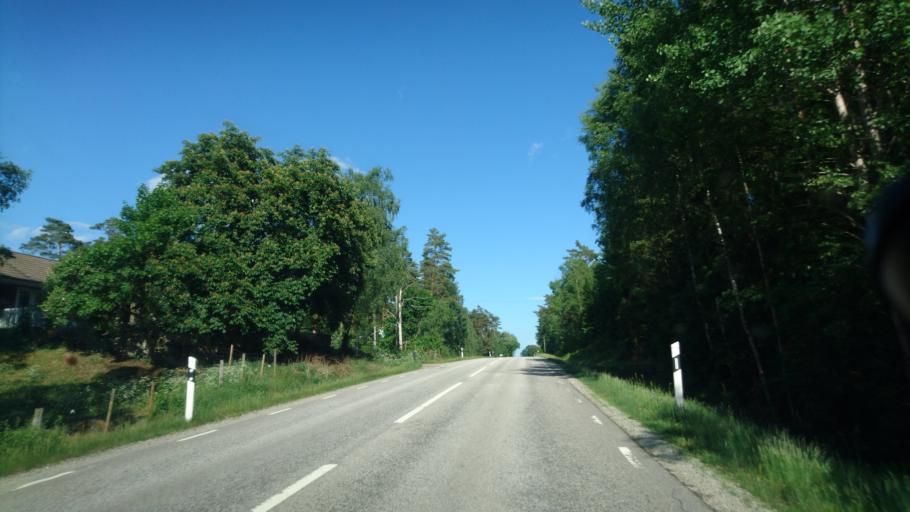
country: SE
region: Skane
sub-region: Osby Kommun
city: Lonsboda
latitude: 56.3915
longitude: 14.4396
